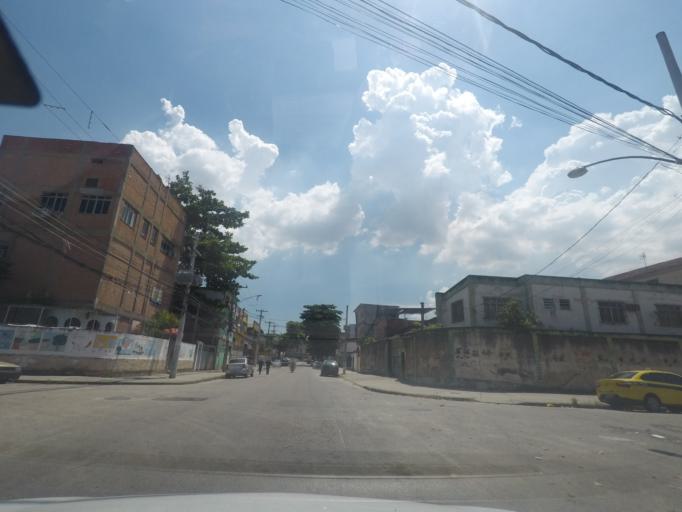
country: BR
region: Rio de Janeiro
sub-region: Rio De Janeiro
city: Rio de Janeiro
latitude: -22.8761
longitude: -43.2546
